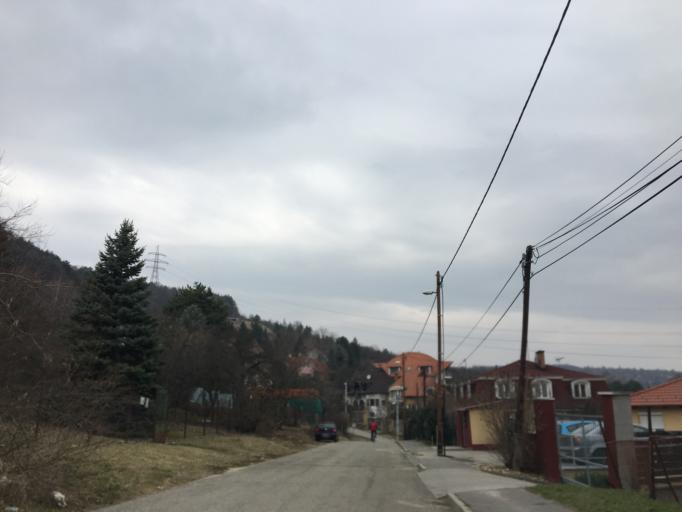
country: HU
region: Pest
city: Urom
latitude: 47.5951
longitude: 19.0390
